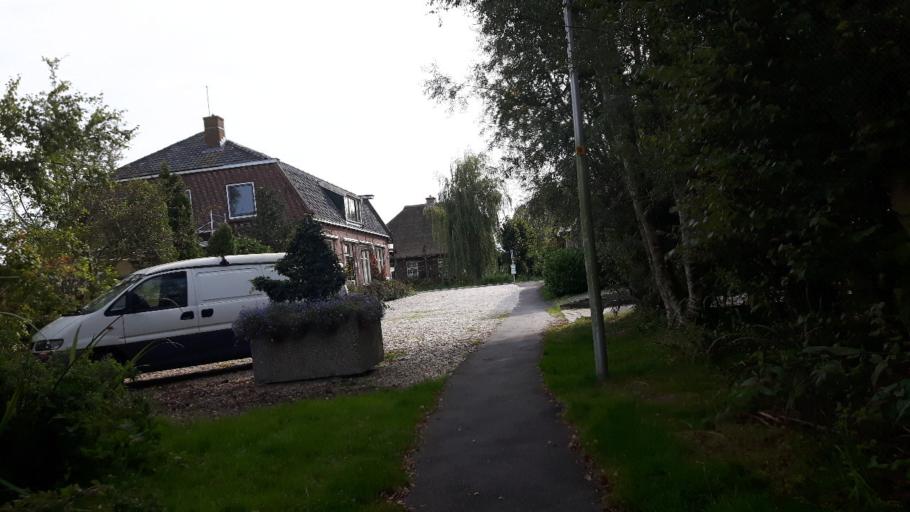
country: NL
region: Utrecht
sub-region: Gemeente De Ronde Venen
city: Mijdrecht
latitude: 52.1658
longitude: 4.8385
